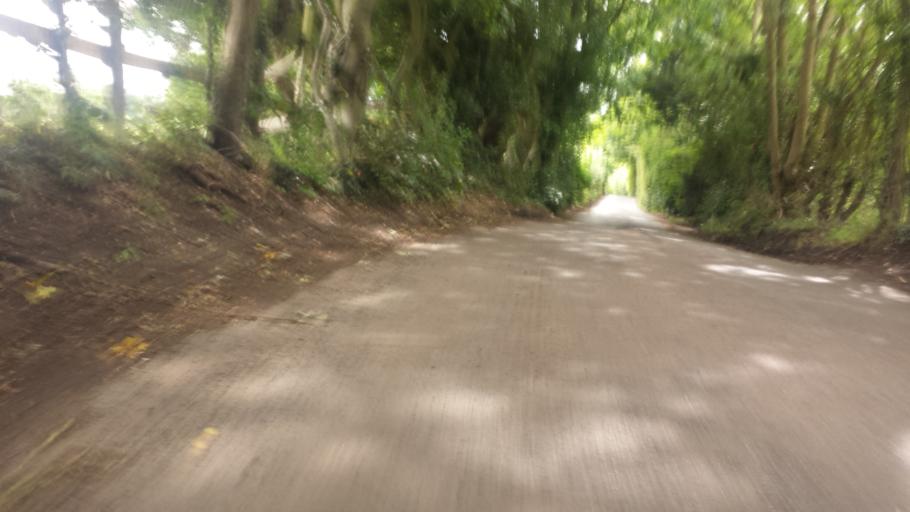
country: GB
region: England
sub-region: Kent
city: Shoreham
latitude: 51.3619
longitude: 0.1532
